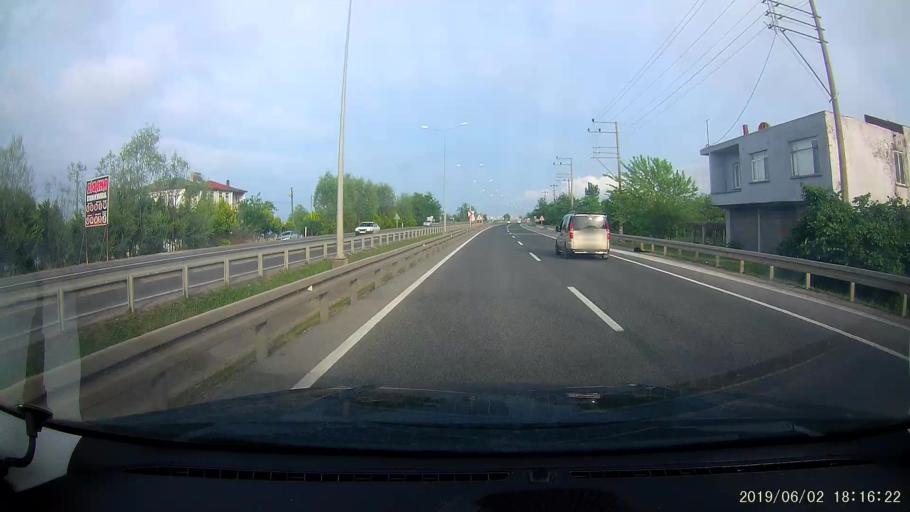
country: TR
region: Ordu
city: Unieh
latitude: 41.1012
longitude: 37.3972
